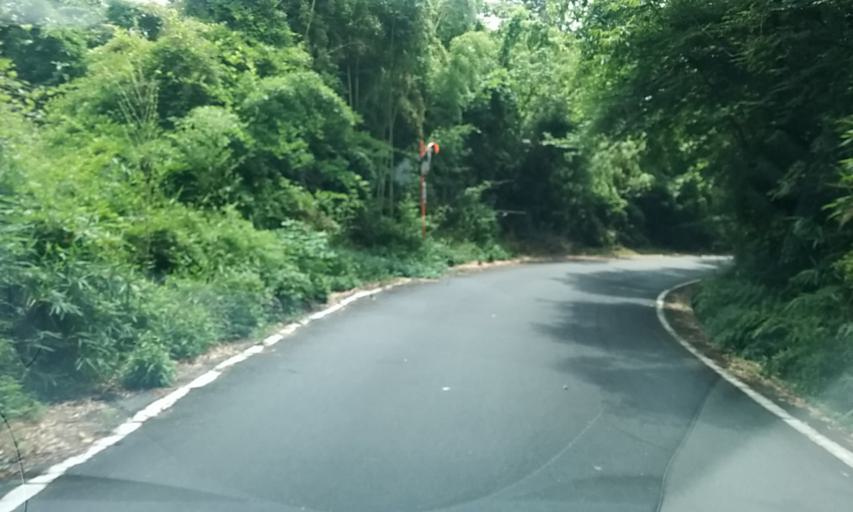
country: JP
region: Kyoto
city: Kameoka
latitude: 35.0892
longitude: 135.4526
